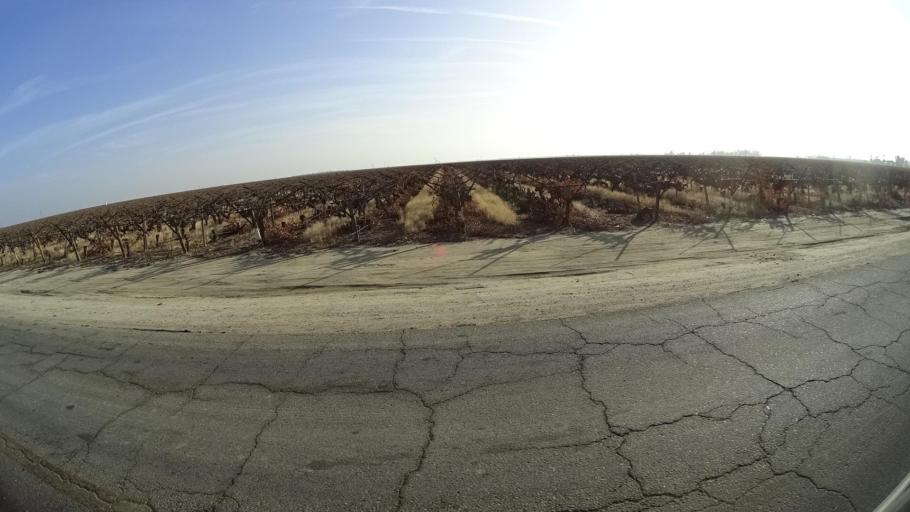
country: US
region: California
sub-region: Kern County
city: Delano
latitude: 35.7823
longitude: -119.1875
